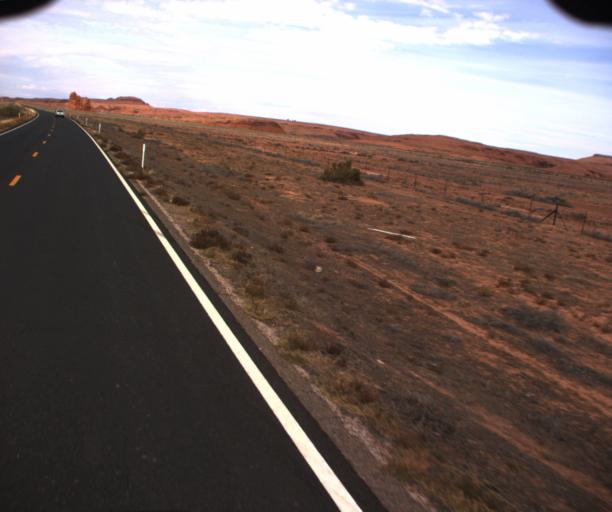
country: US
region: Arizona
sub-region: Apache County
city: Many Farms
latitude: 36.7367
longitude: -109.6344
